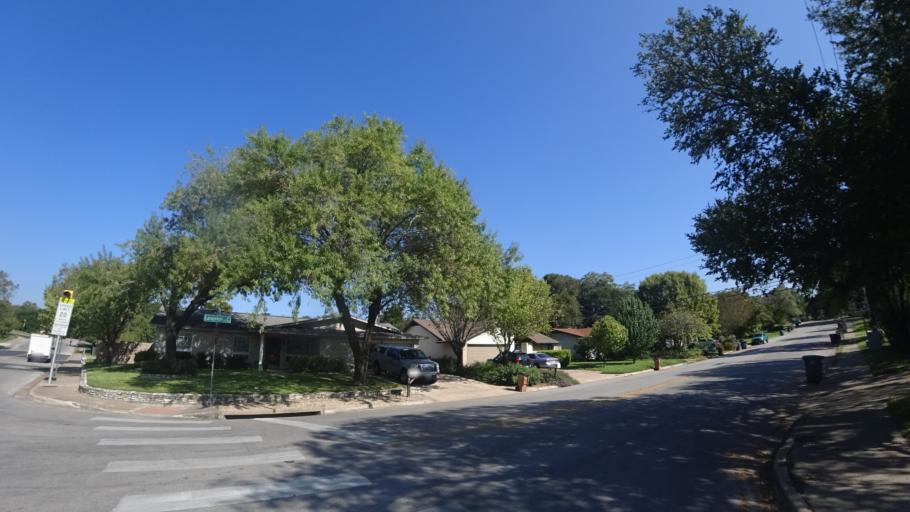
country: US
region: Texas
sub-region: Travis County
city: Austin
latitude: 30.3149
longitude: -97.6739
